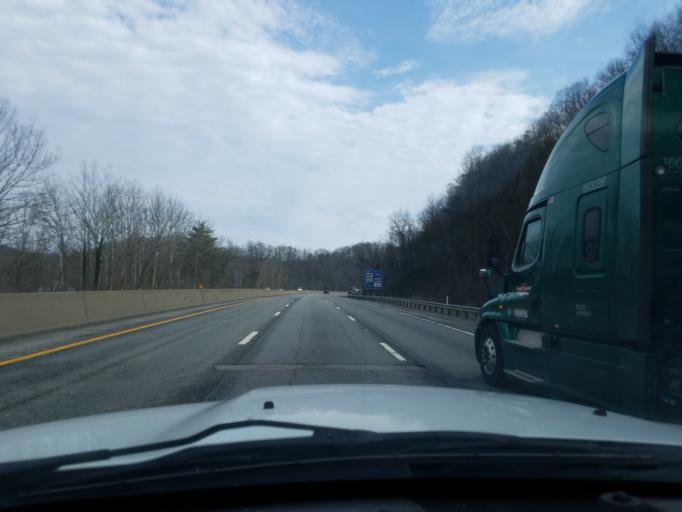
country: US
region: West Virginia
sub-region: Kanawha County
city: Cross Lanes
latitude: 38.4273
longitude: -81.8168
